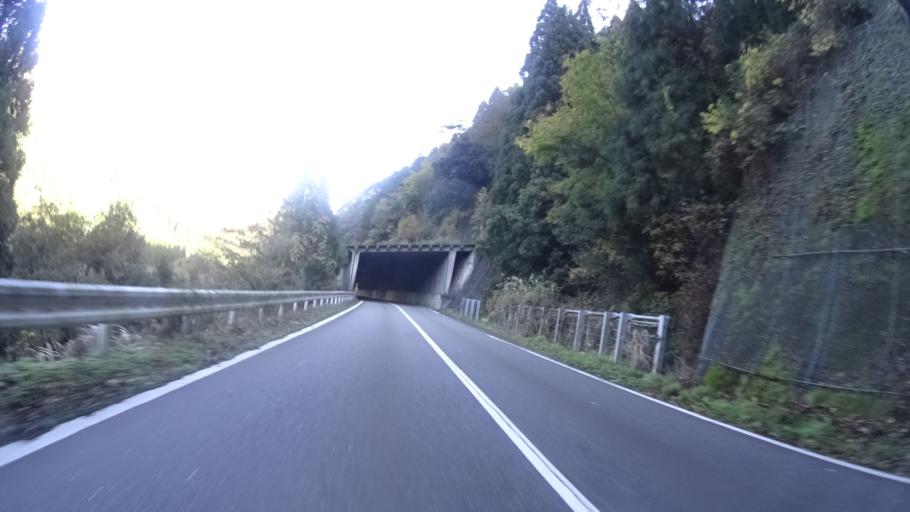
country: JP
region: Fukui
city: Maruoka
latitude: 36.2148
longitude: 136.3526
